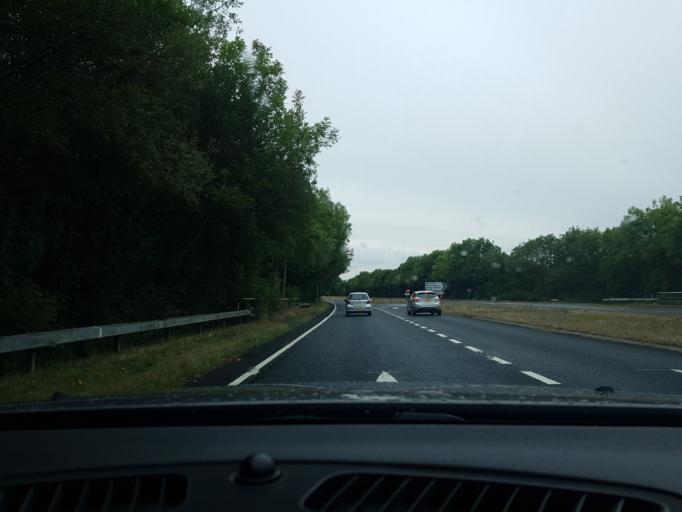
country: GB
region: England
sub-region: Hampshire
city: Odiham
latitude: 51.2601
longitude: -0.9299
